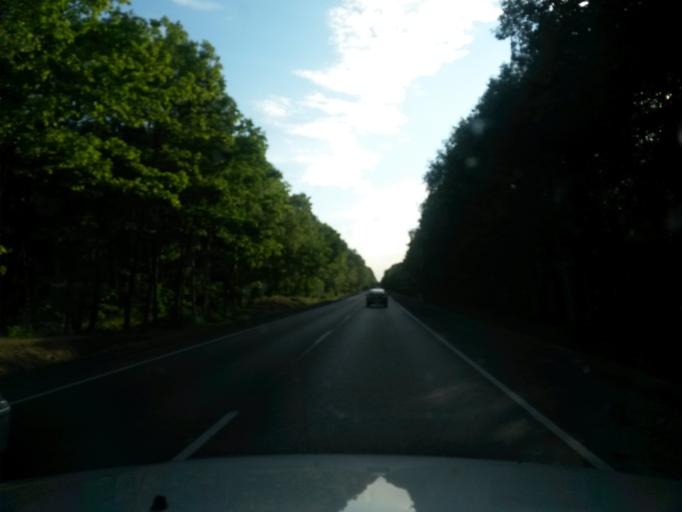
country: PL
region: Lodz Voivodeship
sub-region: Powiat belchatowski
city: Szczercow
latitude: 51.3355
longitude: 19.1666
